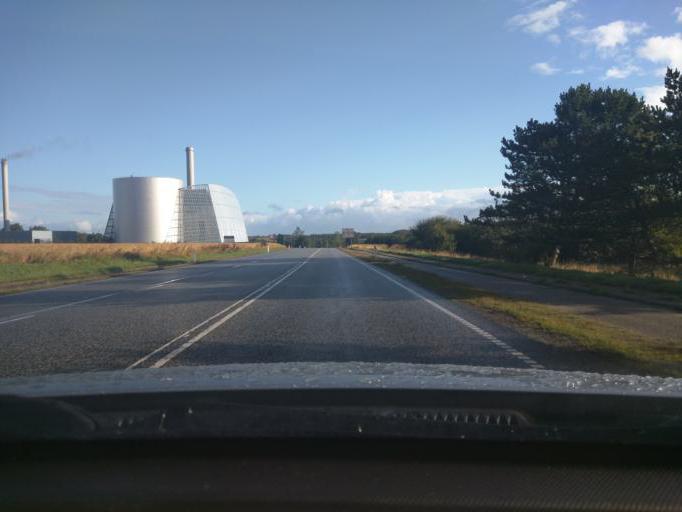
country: DK
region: Central Jutland
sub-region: Viborg Kommune
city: Viborg
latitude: 56.4712
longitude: 9.4154
